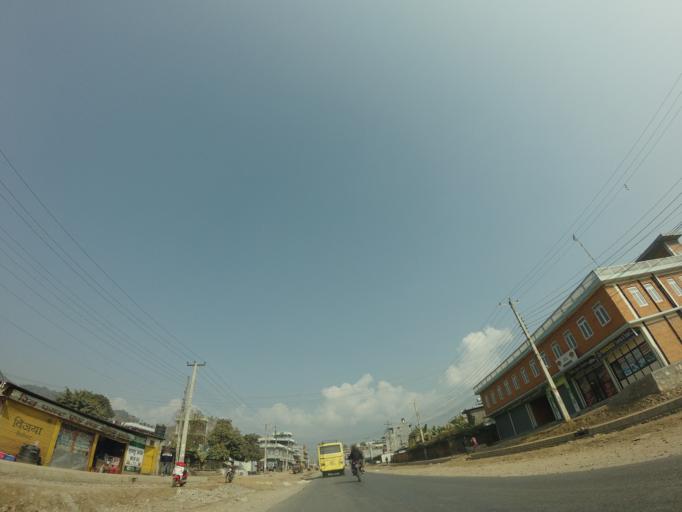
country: NP
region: Western Region
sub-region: Gandaki Zone
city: Pokhara
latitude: 28.2338
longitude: 83.9829
